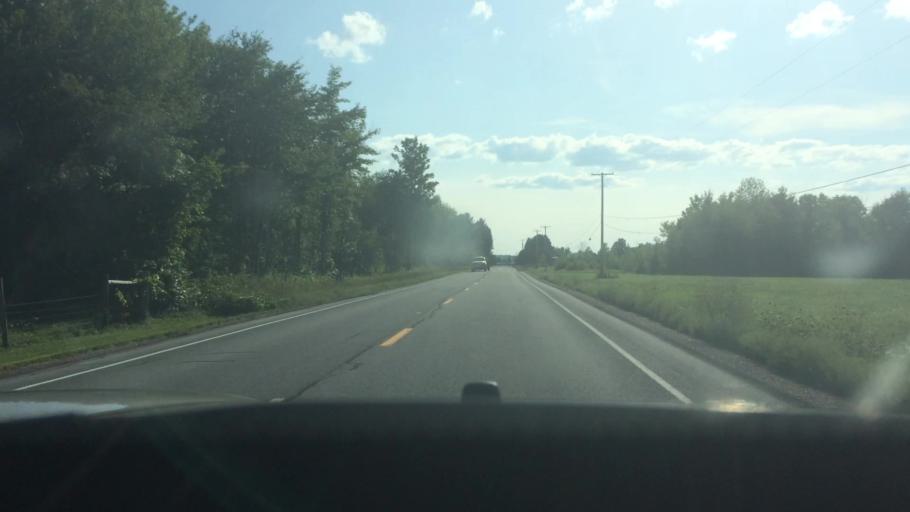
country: CA
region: Ontario
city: Cornwall
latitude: 44.7323
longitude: -74.6020
